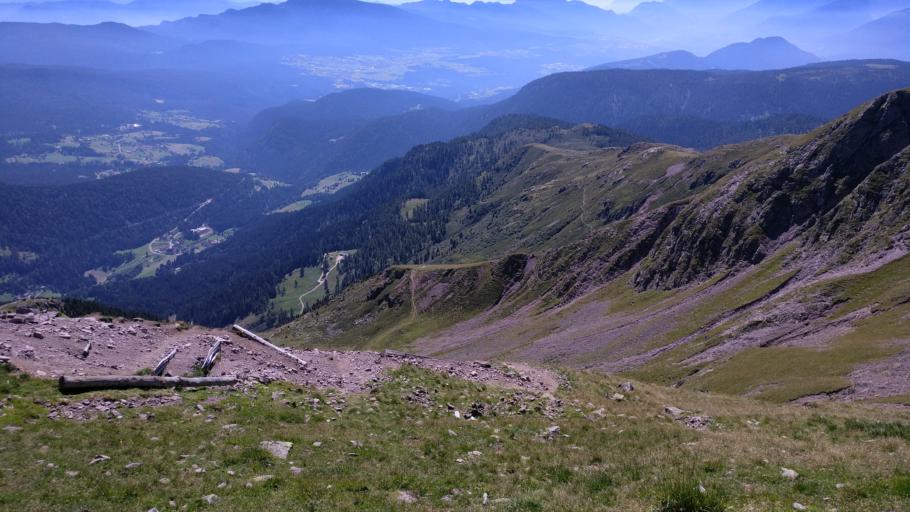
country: IT
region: Trentino-Alto Adige
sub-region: Bolzano
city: Senale
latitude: 46.5345
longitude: 11.0859
